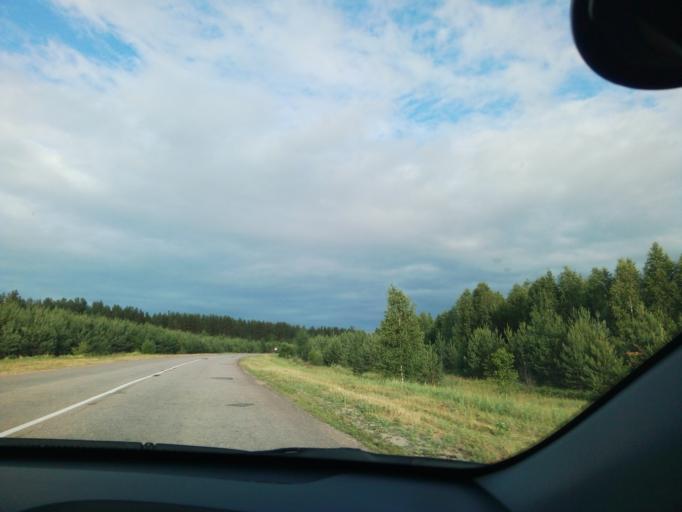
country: RU
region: Rjazan
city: Yermish'
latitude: 54.7528
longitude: 42.3560
